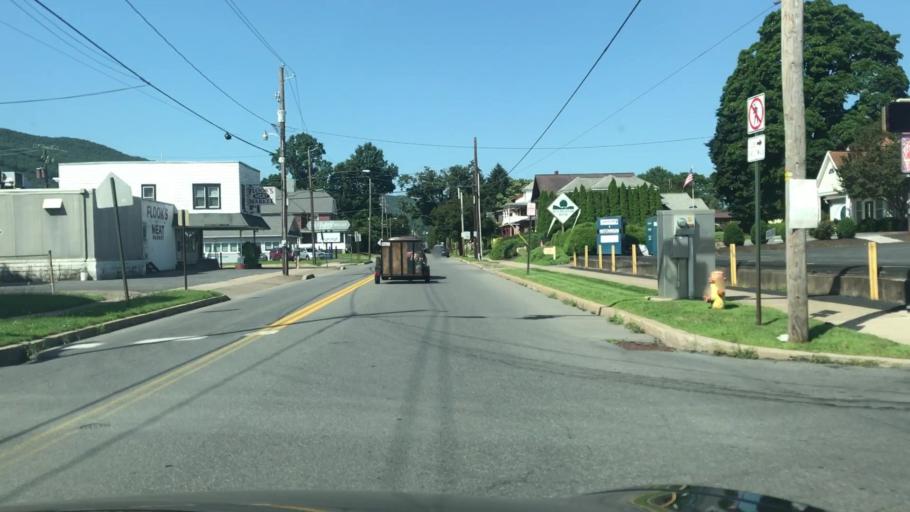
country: US
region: Pennsylvania
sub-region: Lycoming County
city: South Williamsport
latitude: 41.2311
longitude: -77.0013
